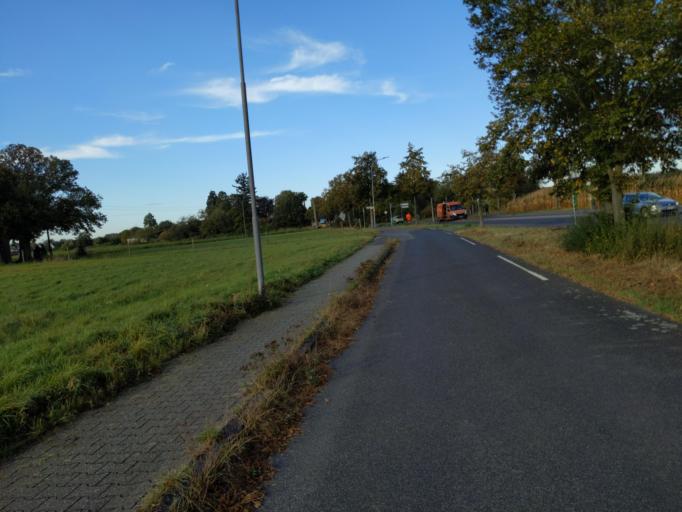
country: DE
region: North Rhine-Westphalia
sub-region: Regierungsbezirk Dusseldorf
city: Kaarst
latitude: 51.2198
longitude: 6.5938
